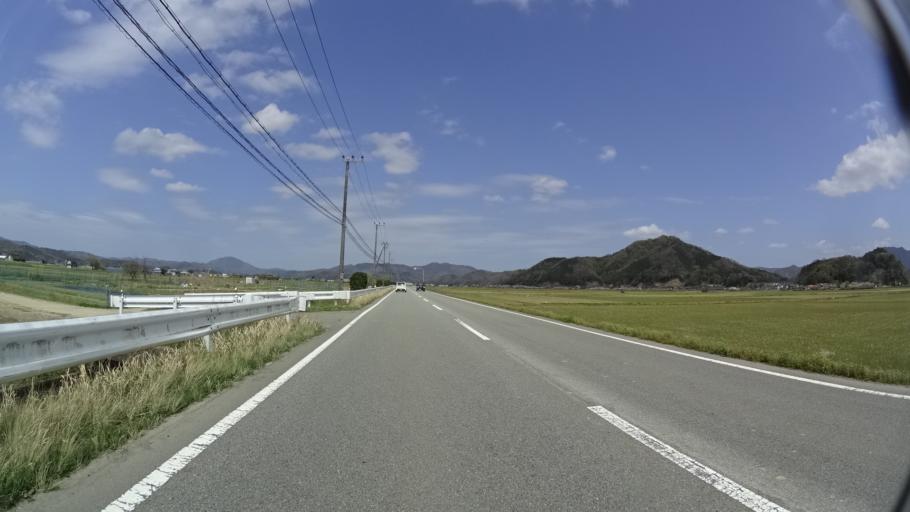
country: JP
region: Hyogo
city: Toyooka
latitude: 35.5089
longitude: 134.8400
